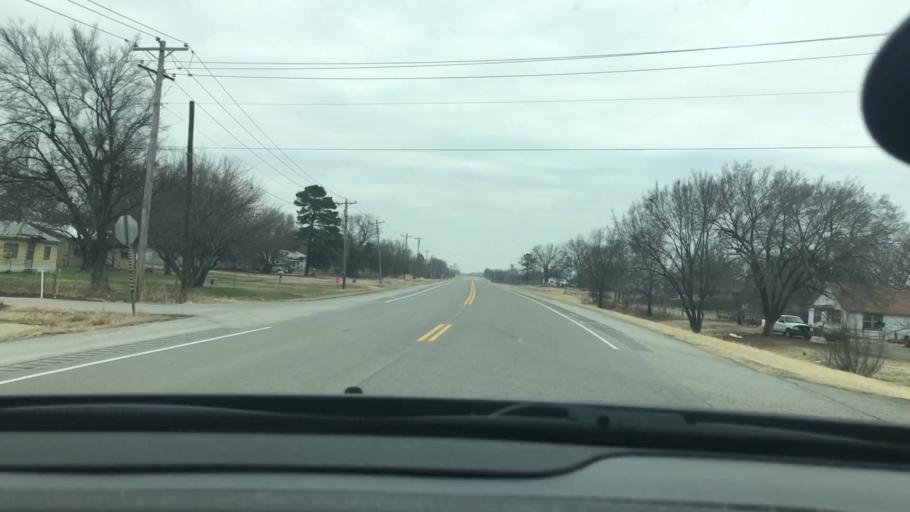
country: US
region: Oklahoma
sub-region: Carter County
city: Healdton
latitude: 34.4053
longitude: -97.5090
